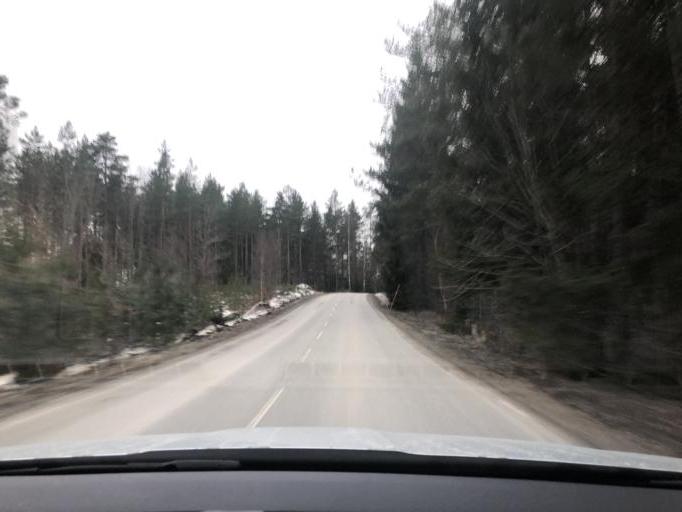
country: SE
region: Stockholm
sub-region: Botkyrka Kommun
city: Tullinge
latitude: 59.1689
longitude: 17.9133
